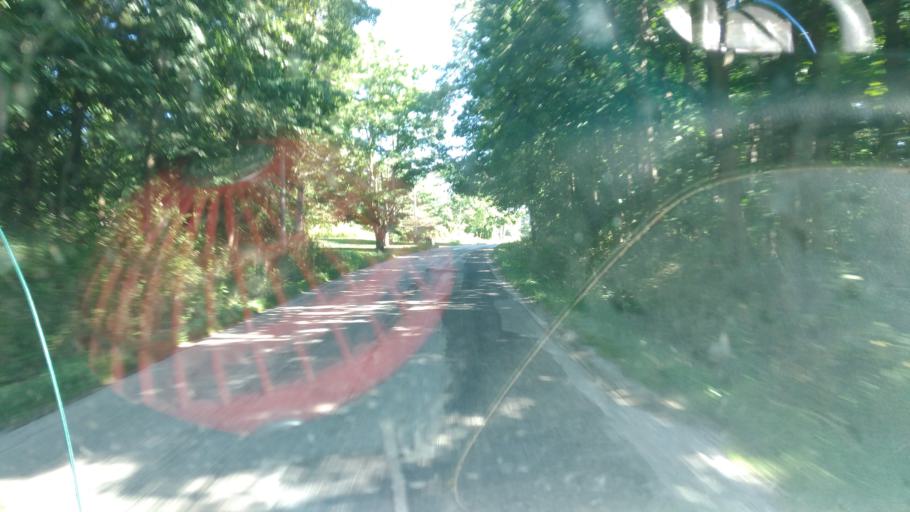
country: US
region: Ohio
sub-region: Ashland County
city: Ashland
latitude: 40.8959
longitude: -82.4311
